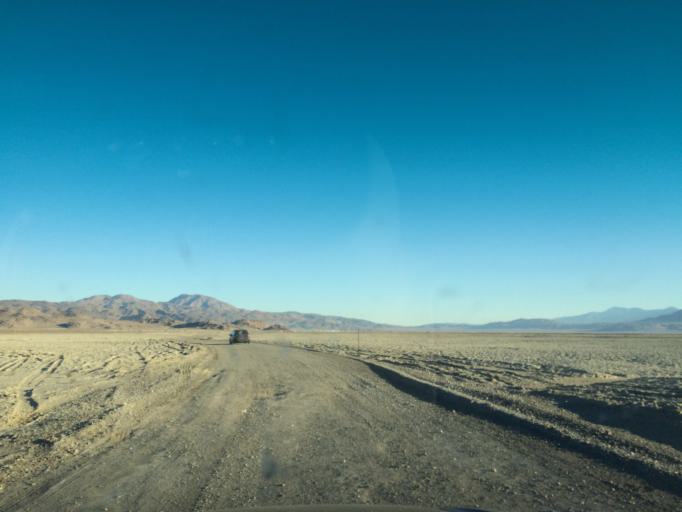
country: US
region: California
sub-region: San Bernardino County
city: Searles Valley
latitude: 35.6519
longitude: -117.3770
